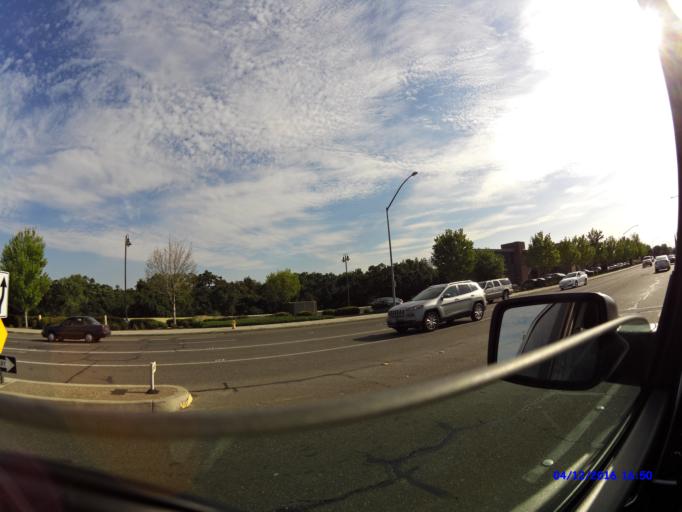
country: US
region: California
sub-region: Stanislaus County
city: Modesto
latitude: 37.6488
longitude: -120.9765
